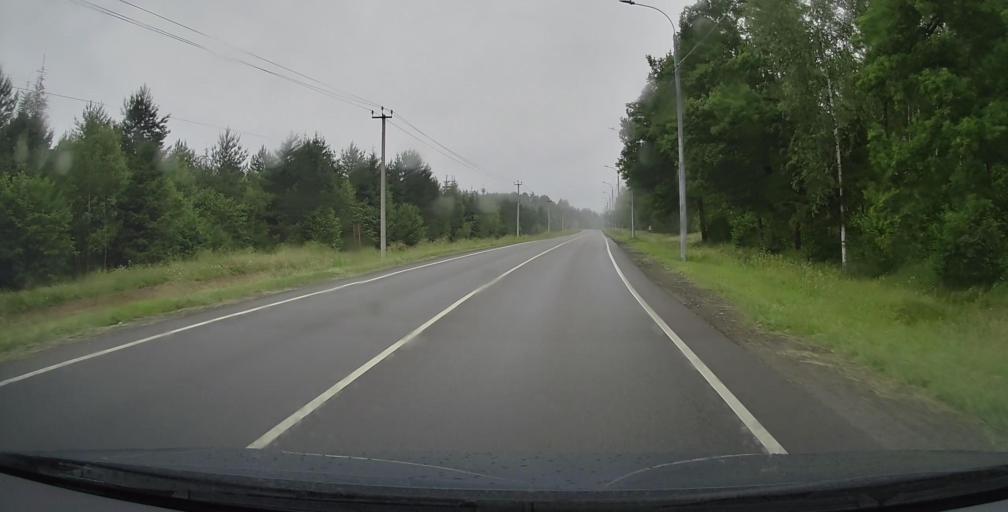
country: RU
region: Moskovskaya
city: Selyatino
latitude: 55.4206
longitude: 36.9760
